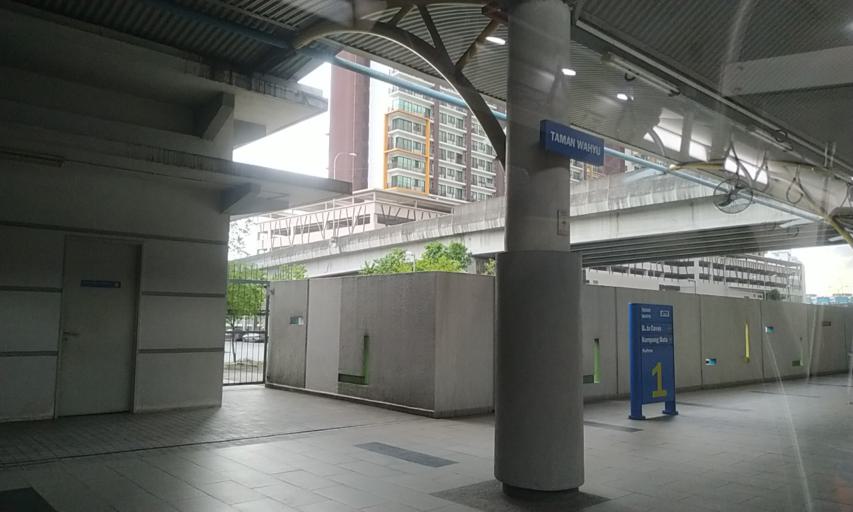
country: MY
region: Kuala Lumpur
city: Kuala Lumpur
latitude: 3.2143
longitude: 101.6723
